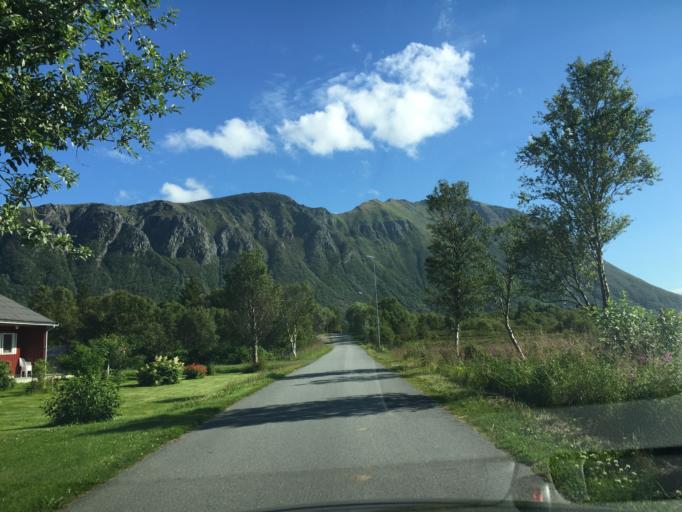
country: NO
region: Nordland
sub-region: Vagan
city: Kabelvag
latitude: 68.3915
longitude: 14.4683
